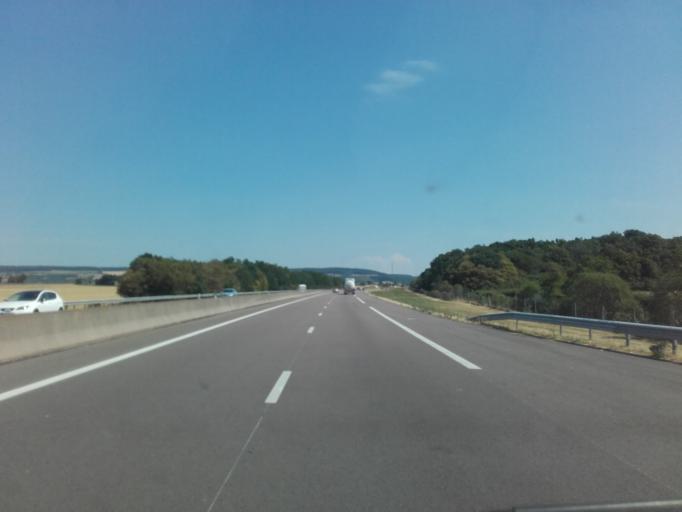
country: FR
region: Bourgogne
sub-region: Departement de la Cote-d'Or
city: Vitteaux
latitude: 47.3533
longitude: 4.4442
